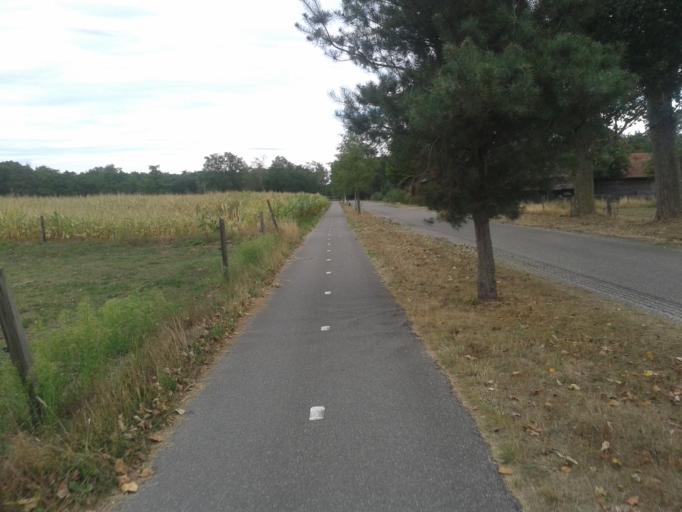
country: NL
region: North Brabant
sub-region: Gemeente Oisterwijk
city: Oisterwijk
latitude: 51.5508
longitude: 5.2037
